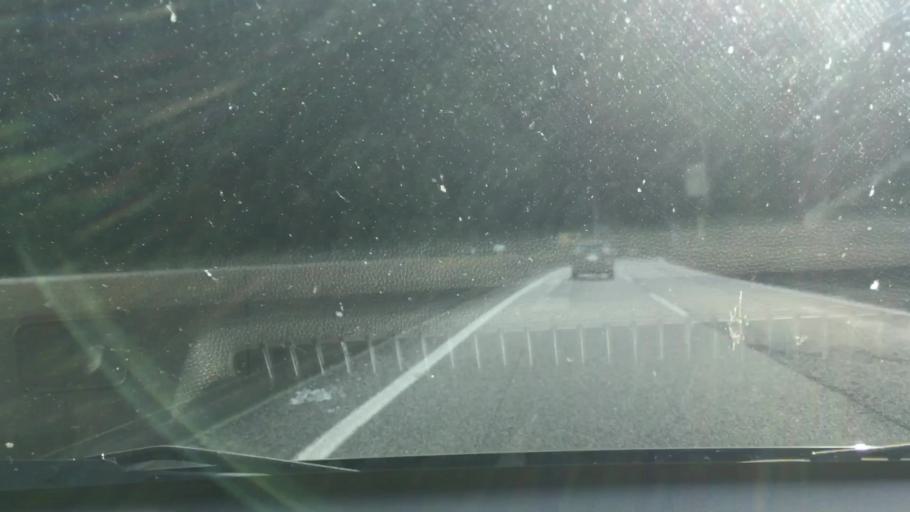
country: JP
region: Kumamoto
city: Yatsushiro
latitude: 32.4253
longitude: 130.7021
